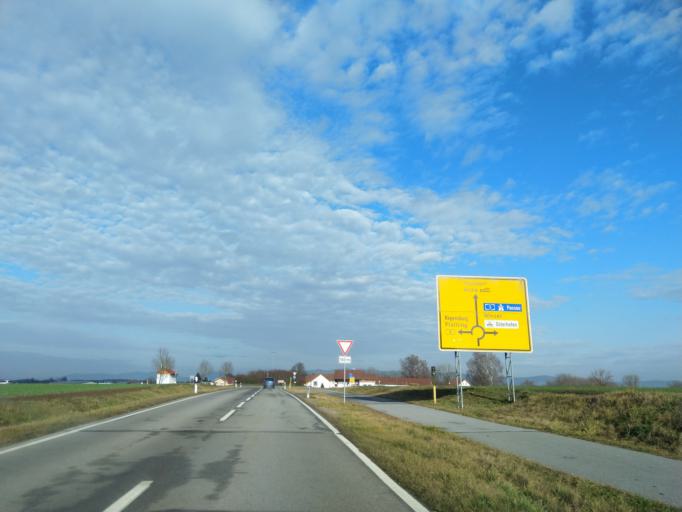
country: DE
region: Bavaria
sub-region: Lower Bavaria
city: Osterhofen
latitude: 48.7156
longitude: 13.0149
